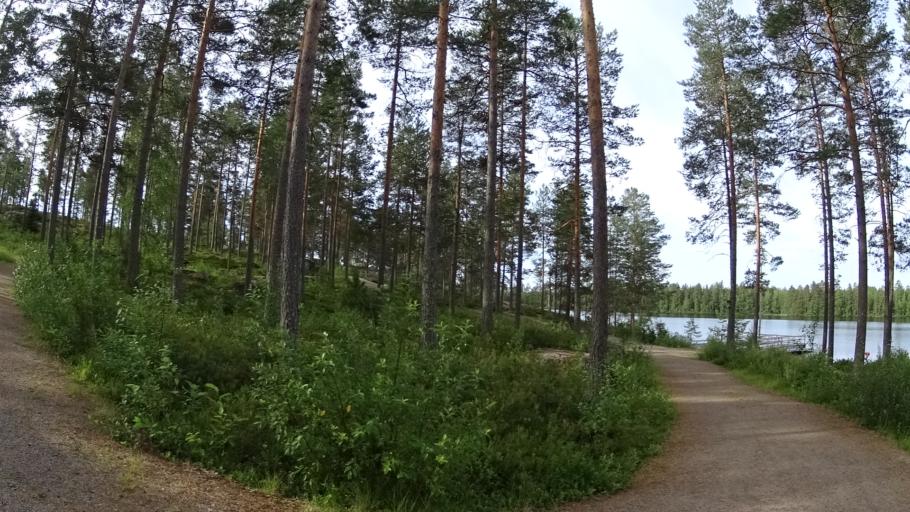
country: FI
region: Southern Ostrobothnia
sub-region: Kuusiokunnat
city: AEhtaeri
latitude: 62.5364
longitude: 24.1794
